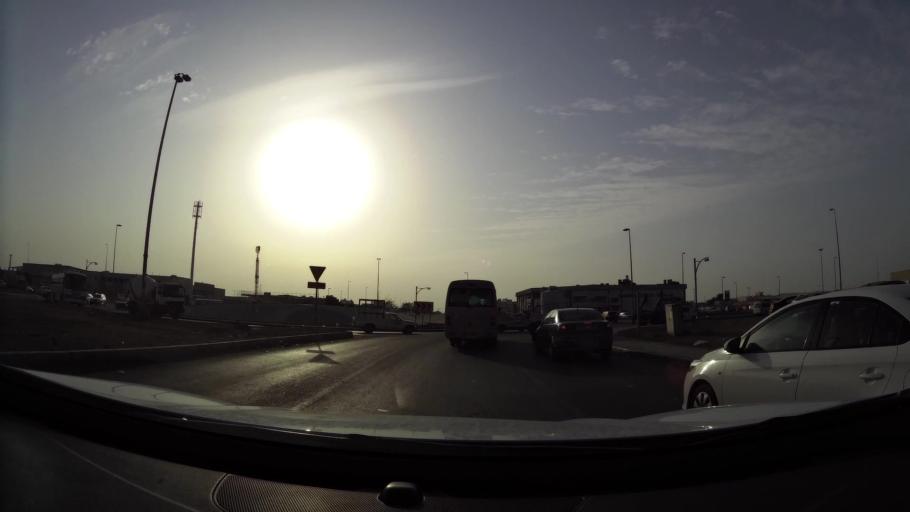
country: AE
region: Abu Dhabi
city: Abu Dhabi
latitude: 24.3689
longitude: 54.5119
